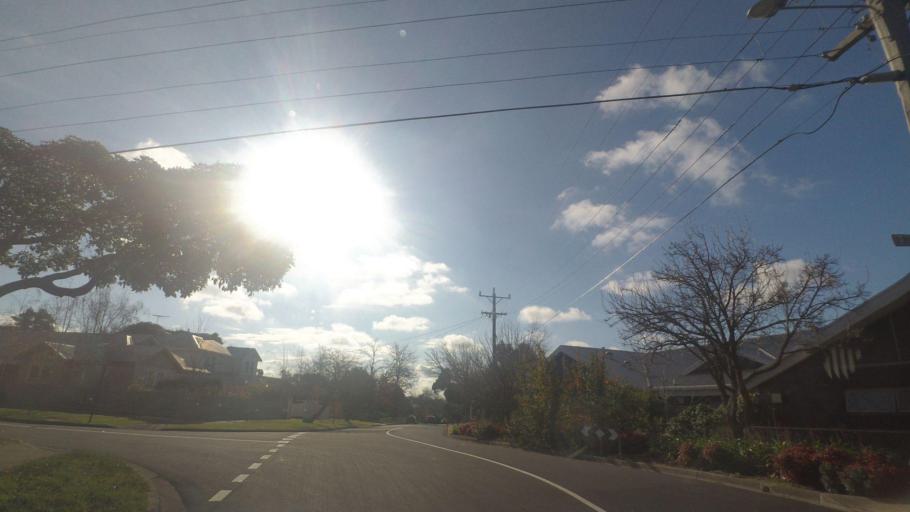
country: AU
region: Victoria
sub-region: Whitehorse
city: Mont Albert North
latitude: -37.8102
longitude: 145.1092
